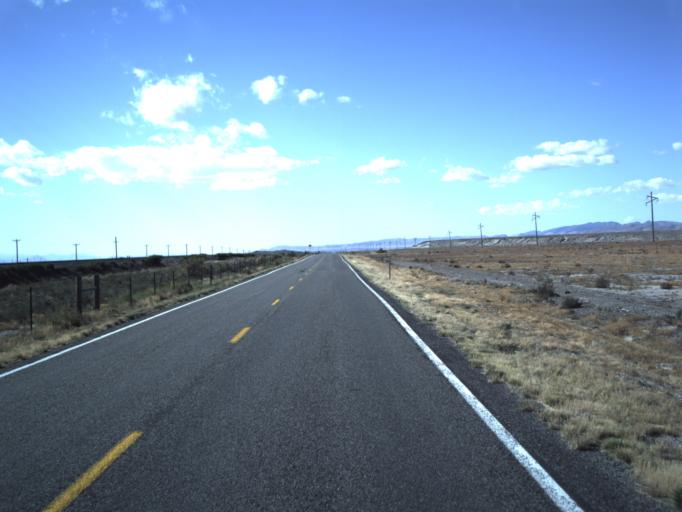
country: US
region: Utah
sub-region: Millard County
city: Delta
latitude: 39.1925
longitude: -112.6928
